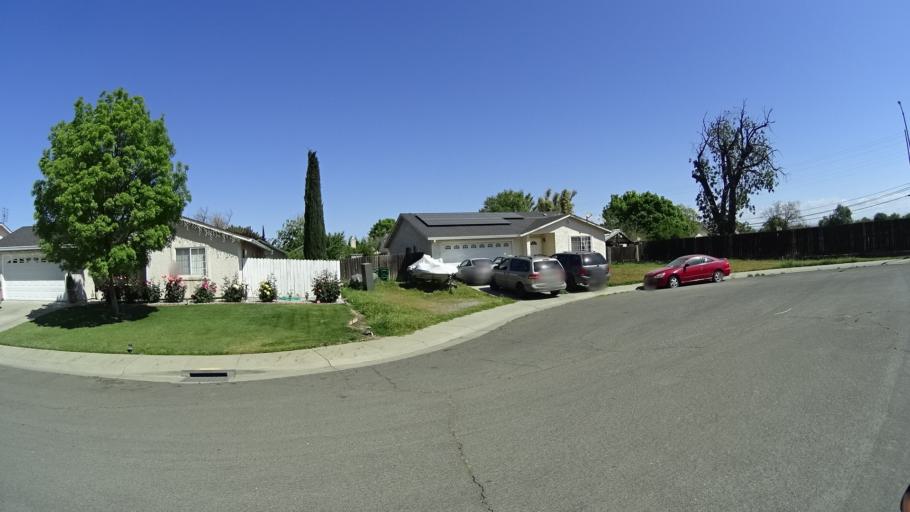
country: US
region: California
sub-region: Glenn County
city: Orland
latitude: 39.7562
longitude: -122.1983
